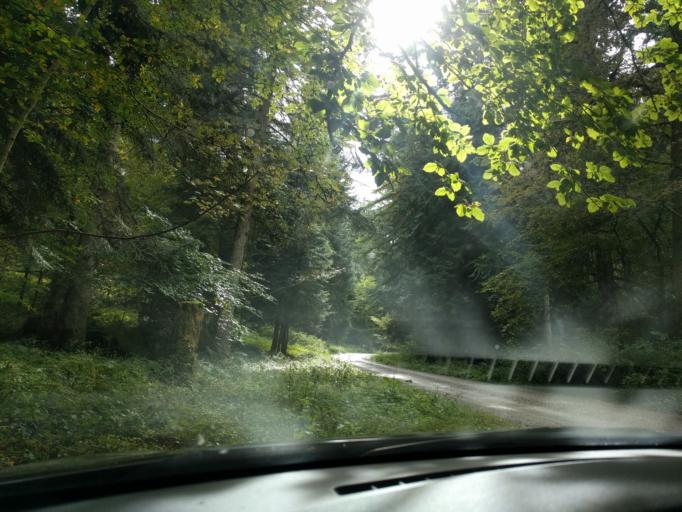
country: CH
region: Bern
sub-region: Bern-Mittelland District
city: Linden
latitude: 46.8612
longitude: 7.6526
